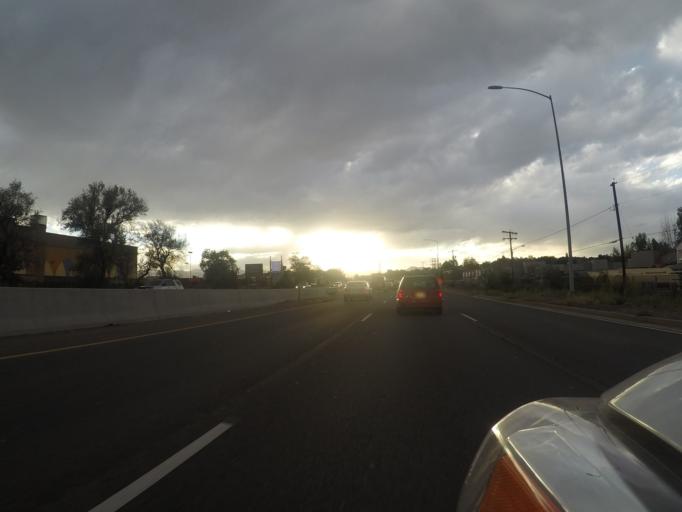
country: US
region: Colorado
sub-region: Arapahoe County
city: Sheridan
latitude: 39.6538
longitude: -105.0081
